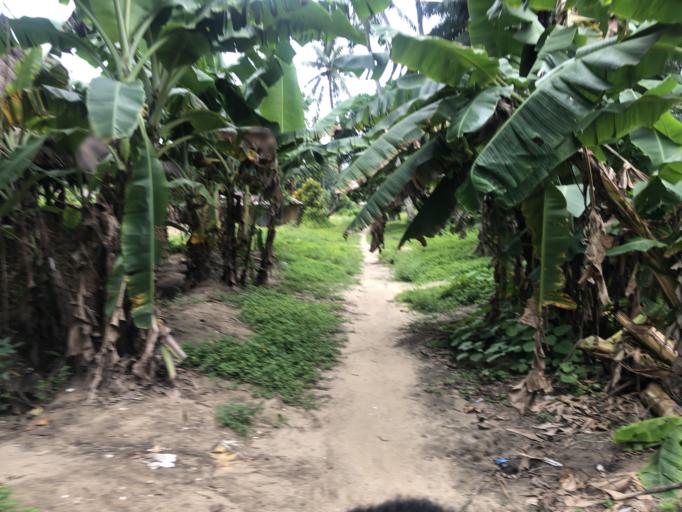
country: SL
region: Southern Province
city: Bonthe
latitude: 7.5216
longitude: -12.5052
